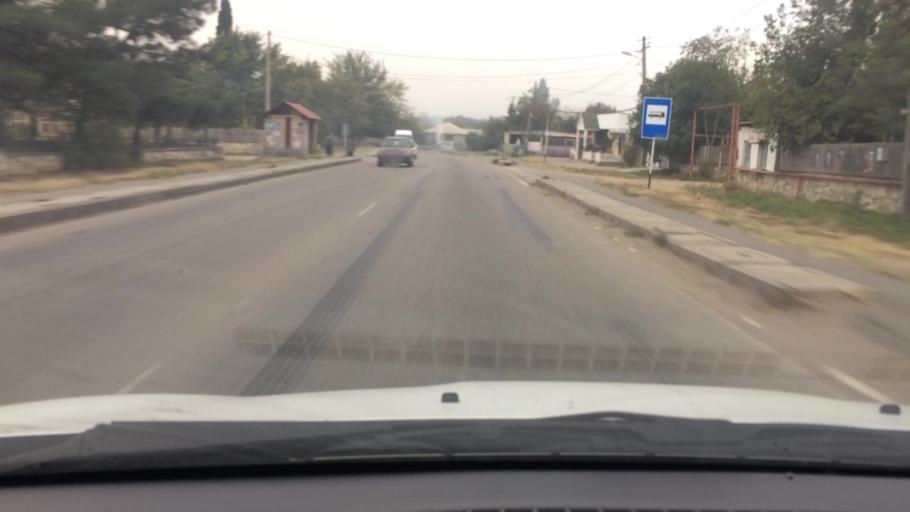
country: GE
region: Kvemo Kartli
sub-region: Marneuli
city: Marneuli
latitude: 41.5827
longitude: 44.7771
